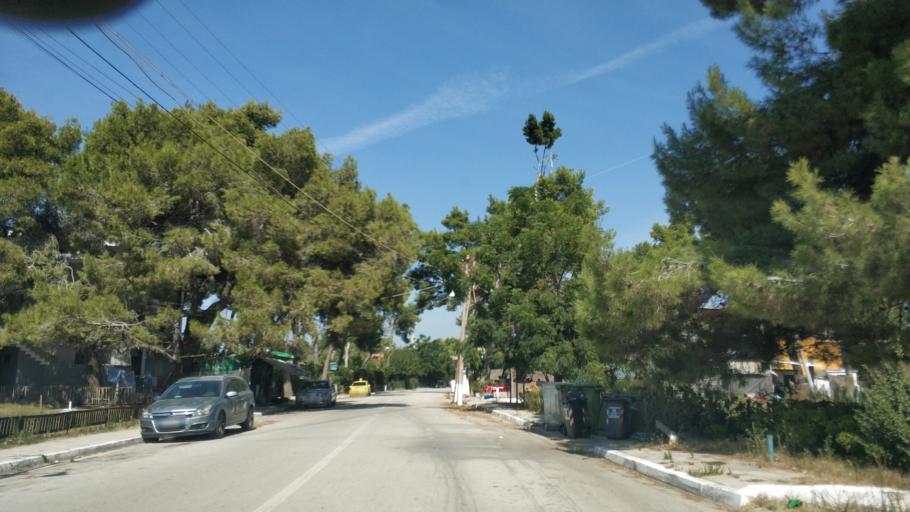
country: AL
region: Fier
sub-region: Rrethi i Lushnjes
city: Divjake
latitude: 40.9704
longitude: 19.4796
